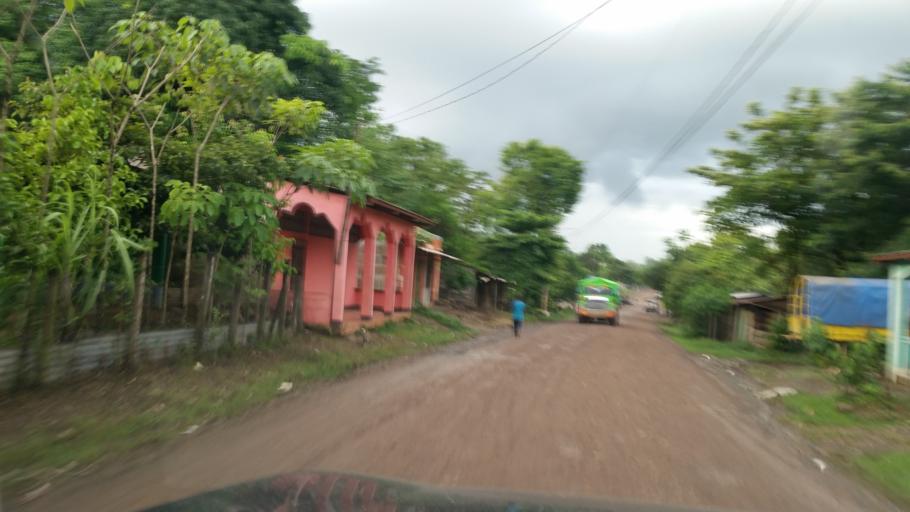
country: NI
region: Atlantico Norte (RAAN)
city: Siuna
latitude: 13.3790
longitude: -84.8622
